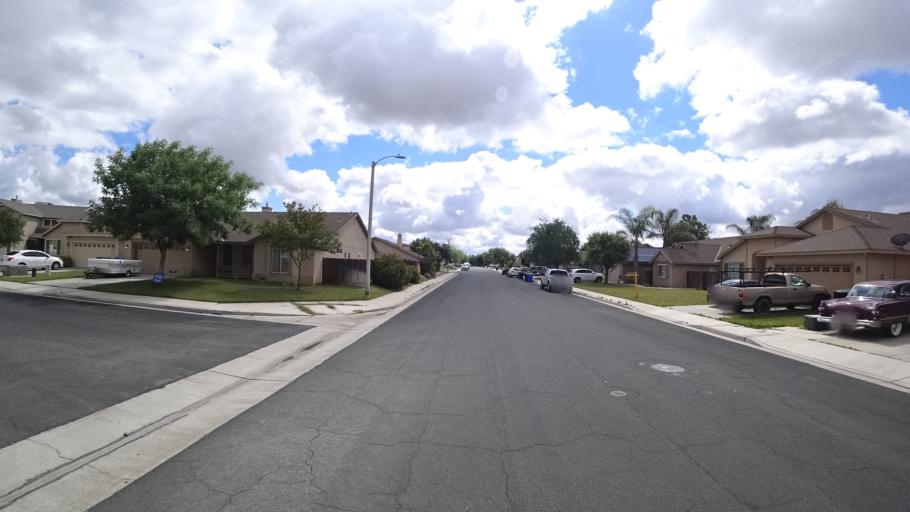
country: US
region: California
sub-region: Kings County
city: Lucerne
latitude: 36.3677
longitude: -119.6587
